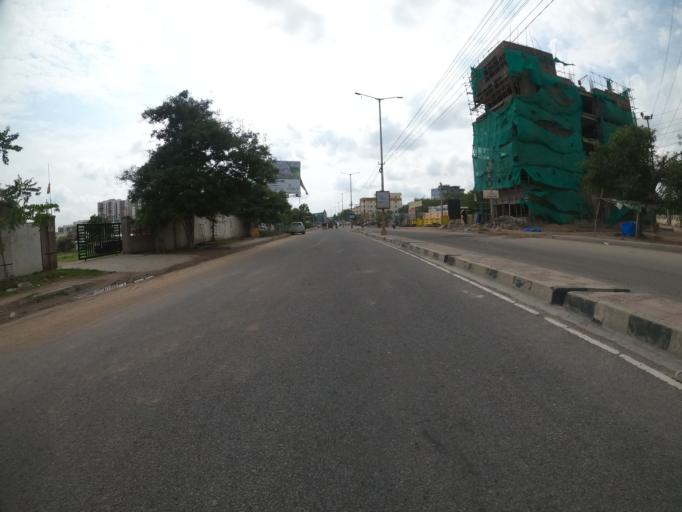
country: IN
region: Telangana
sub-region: Hyderabad
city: Hyderabad
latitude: 17.3828
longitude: 78.3643
